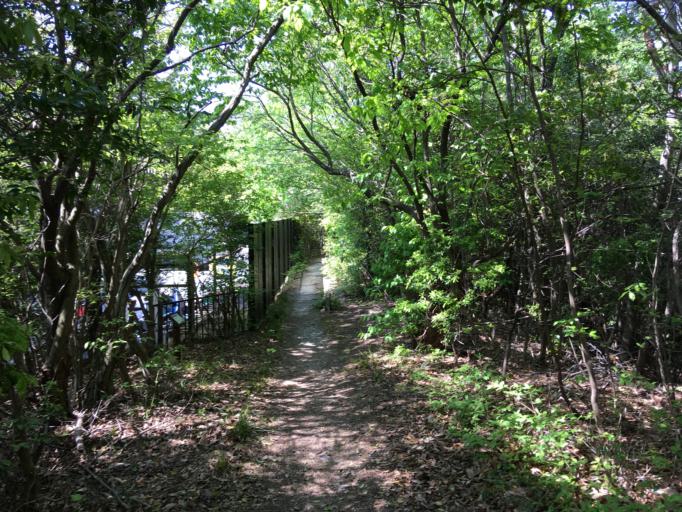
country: JP
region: Nara
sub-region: Ikoma-shi
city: Ikoma
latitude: 34.6880
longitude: 135.7191
